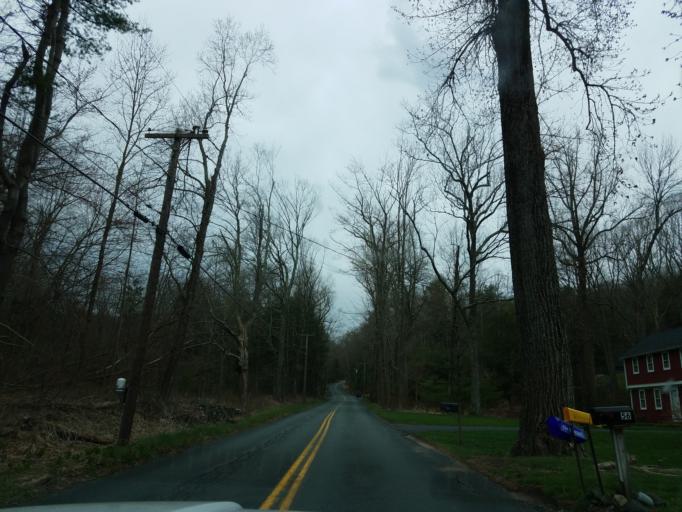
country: US
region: Connecticut
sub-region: Tolland County
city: Somers
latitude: 41.9804
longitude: -72.4217
